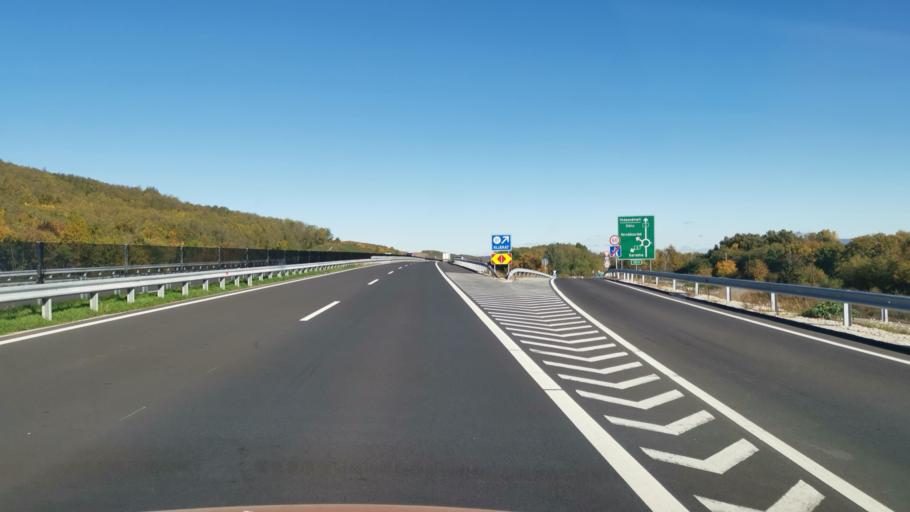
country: HU
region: Borsod-Abauj-Zemplen
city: Gonc
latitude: 48.4688
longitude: 21.2018
